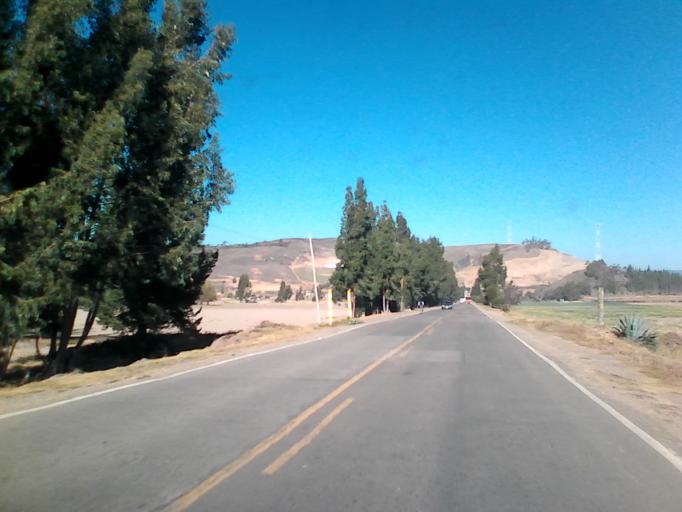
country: CO
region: Boyaca
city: Cucaita
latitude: 5.5420
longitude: -73.4798
